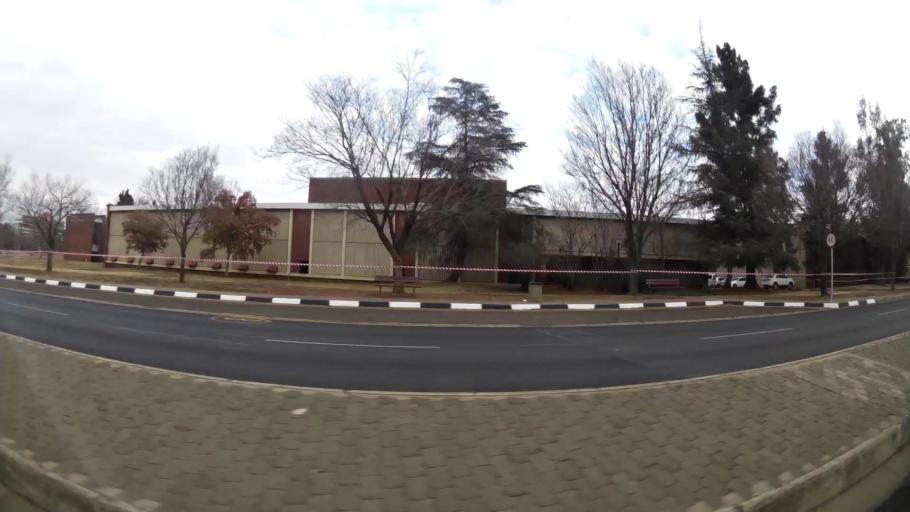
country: ZA
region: Orange Free State
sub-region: Mangaung Metropolitan Municipality
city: Bloemfontein
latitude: -29.1133
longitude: 26.1912
